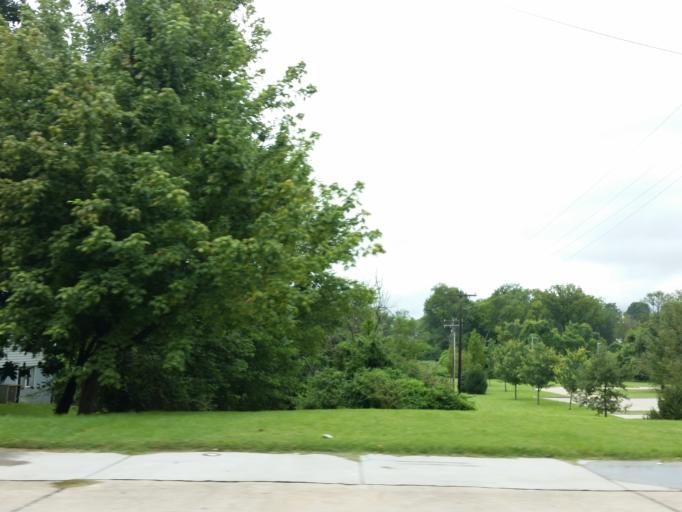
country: US
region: Missouri
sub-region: Cape Girardeau County
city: Cape Girardeau
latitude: 37.3138
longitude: -89.5473
